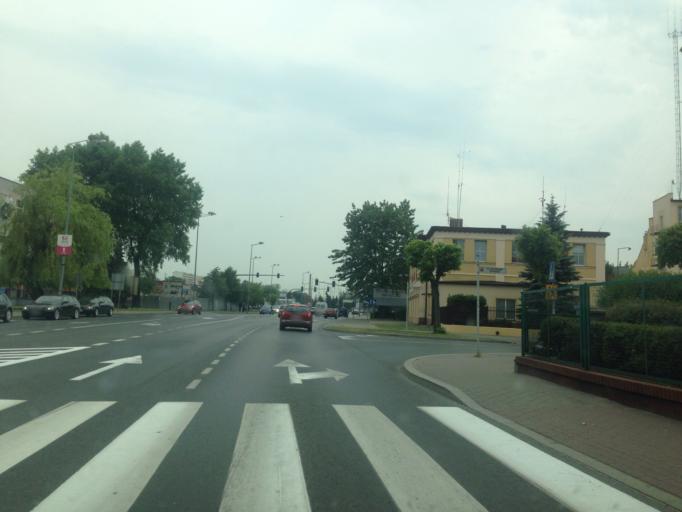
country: PL
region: Kujawsko-Pomorskie
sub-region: Grudziadz
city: Grudziadz
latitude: 53.4910
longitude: 18.7583
